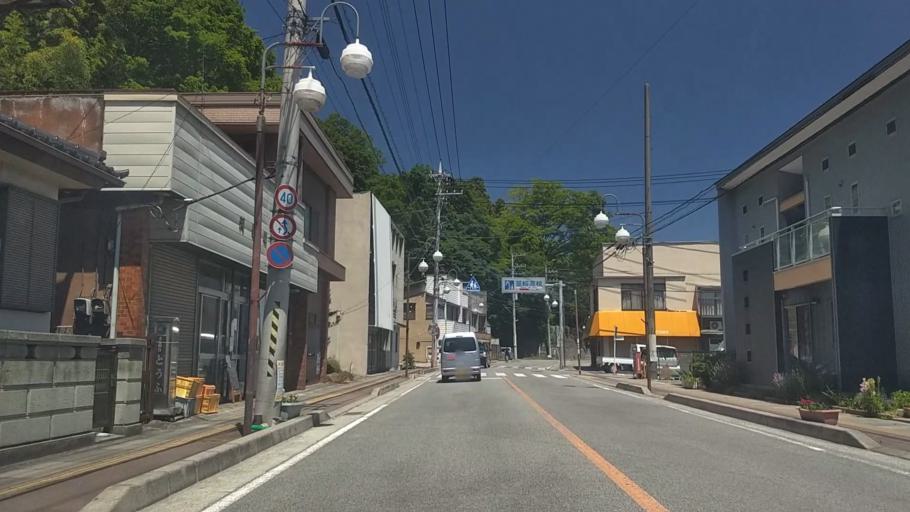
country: JP
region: Yamanashi
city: Nirasaki
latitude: 35.7133
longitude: 138.4486
